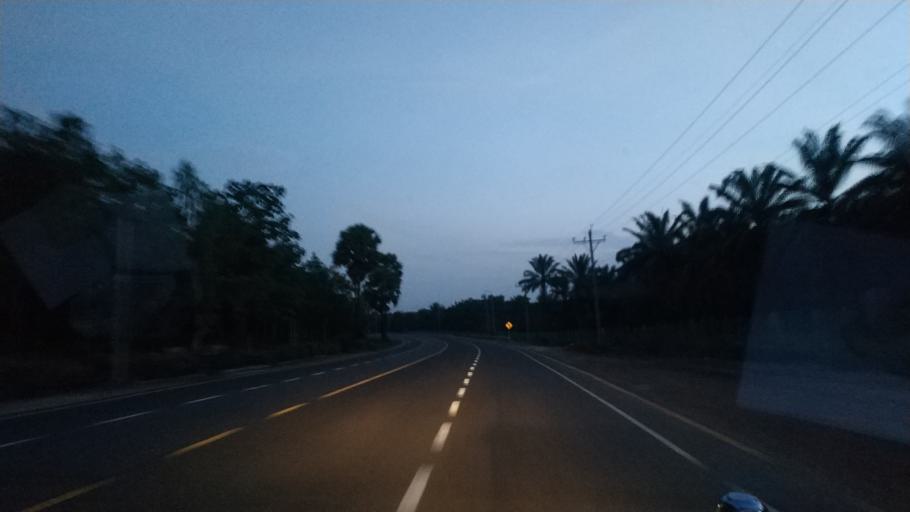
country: MM
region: Mon
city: Kyaikto
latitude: 17.3723
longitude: 97.0506
